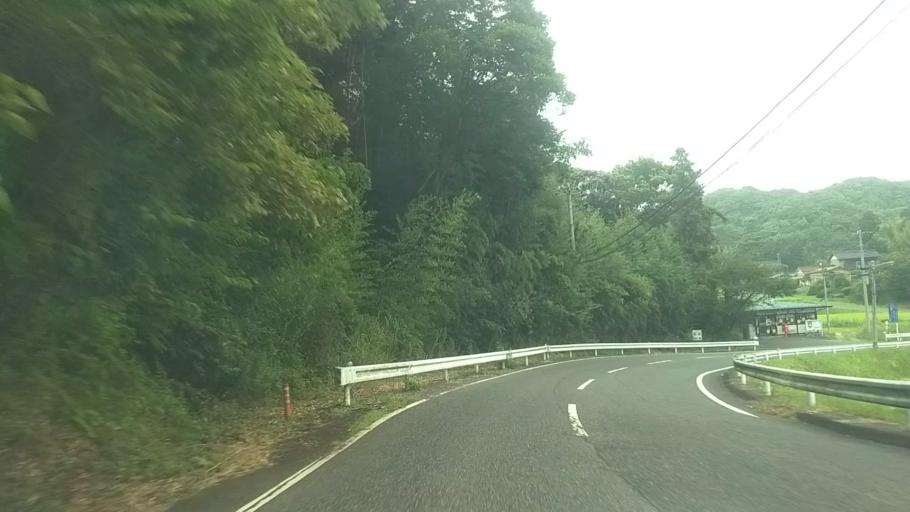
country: JP
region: Chiba
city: Kawaguchi
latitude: 35.2242
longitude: 140.0181
